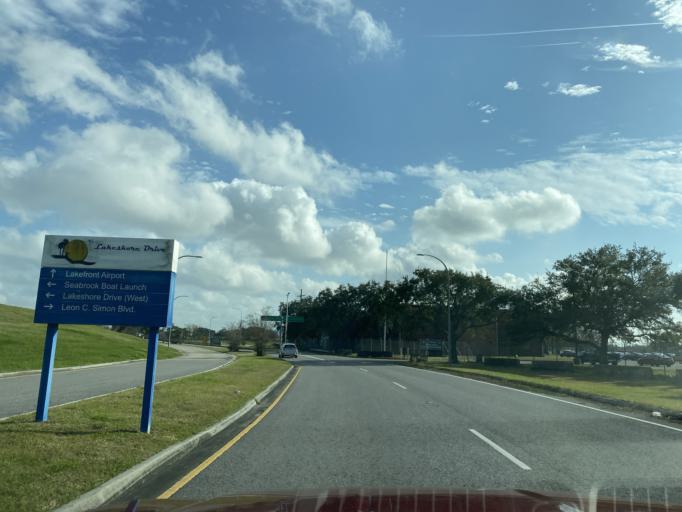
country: US
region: Louisiana
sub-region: Orleans Parish
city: New Orleans
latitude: 30.0323
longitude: -90.0411
